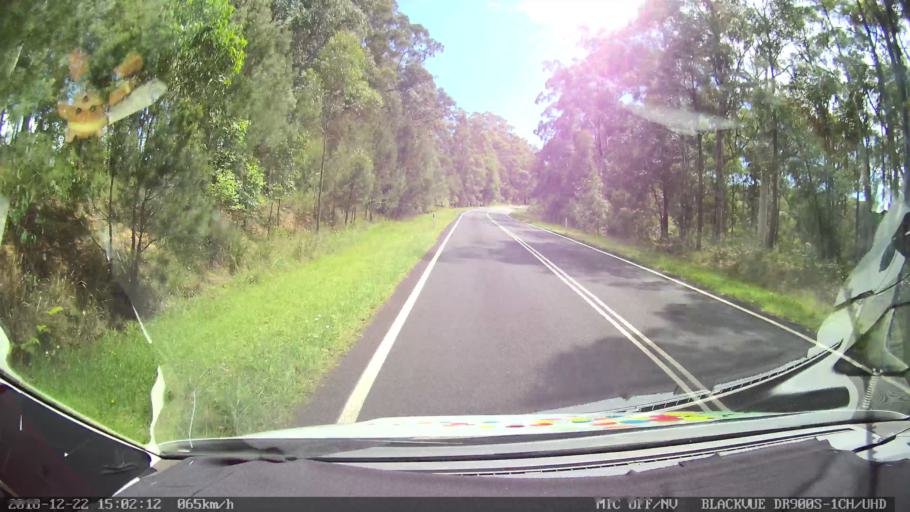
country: AU
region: New South Wales
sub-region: Bellingen
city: Dorrigo
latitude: -30.2601
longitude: 152.4532
